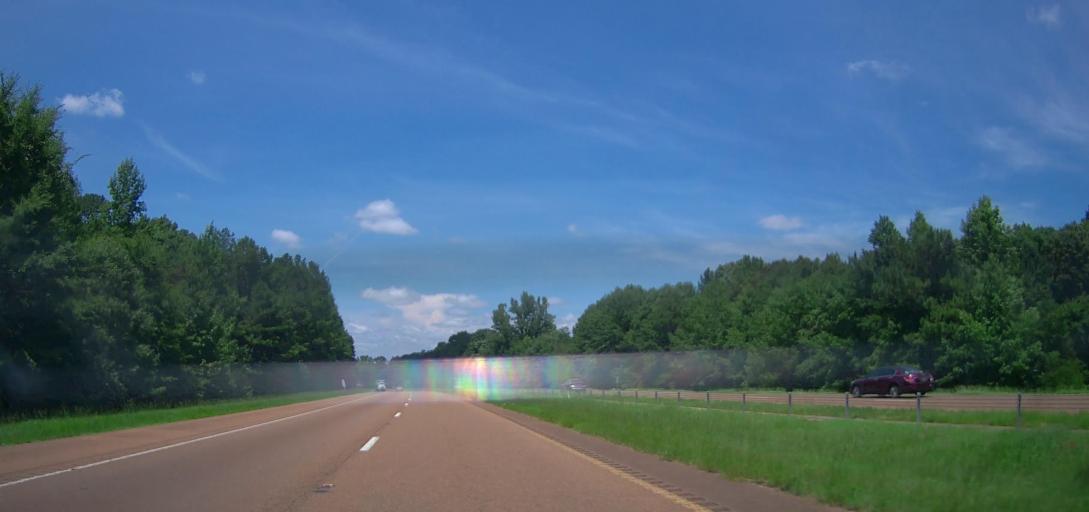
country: US
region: Mississippi
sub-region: Union County
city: New Albany
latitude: 34.4556
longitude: -88.9823
